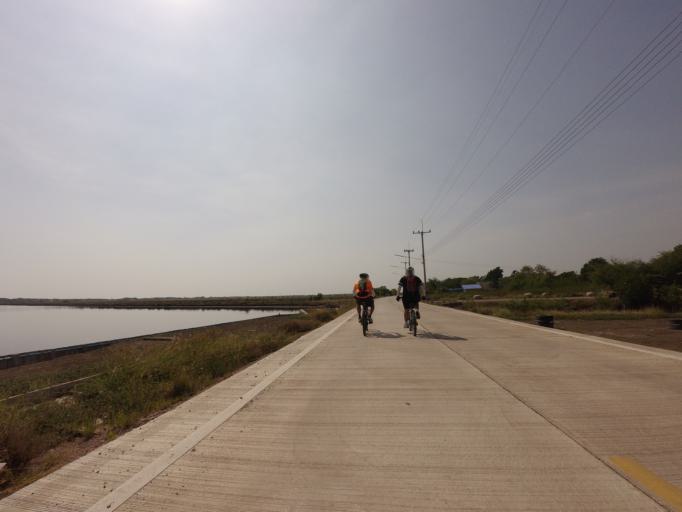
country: TH
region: Samut Sakhon
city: Samut Sakhon
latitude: 13.5142
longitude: 100.4001
